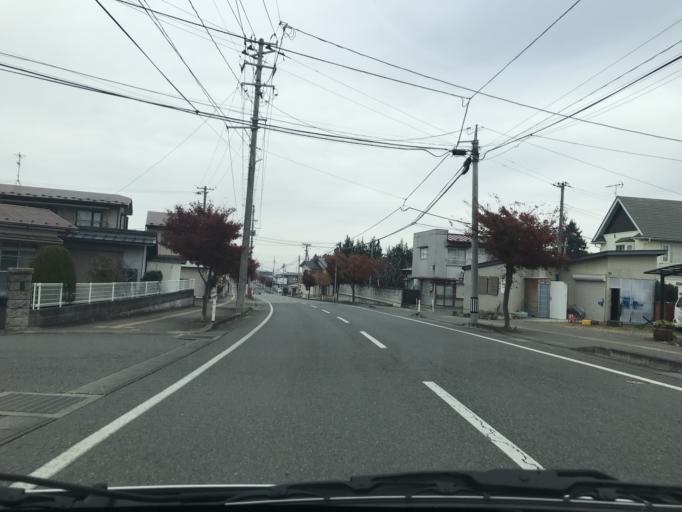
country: JP
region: Iwate
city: Mizusawa
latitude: 39.1226
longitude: 141.1251
